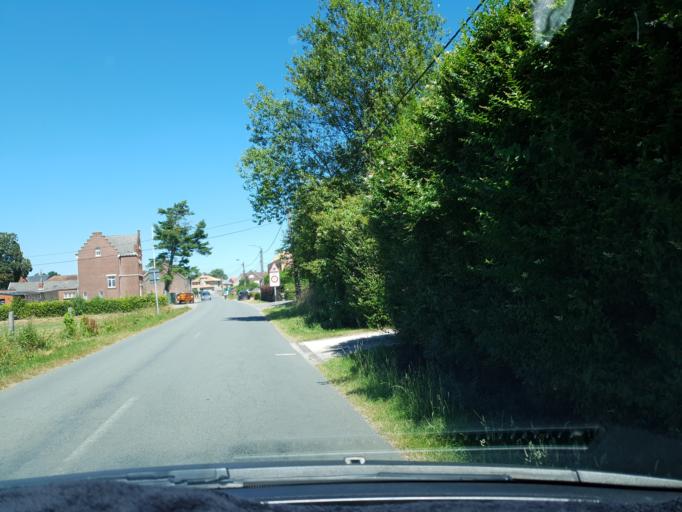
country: BE
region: Flanders
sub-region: Provincie Antwerpen
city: Geel
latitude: 51.1625
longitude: 4.9462
